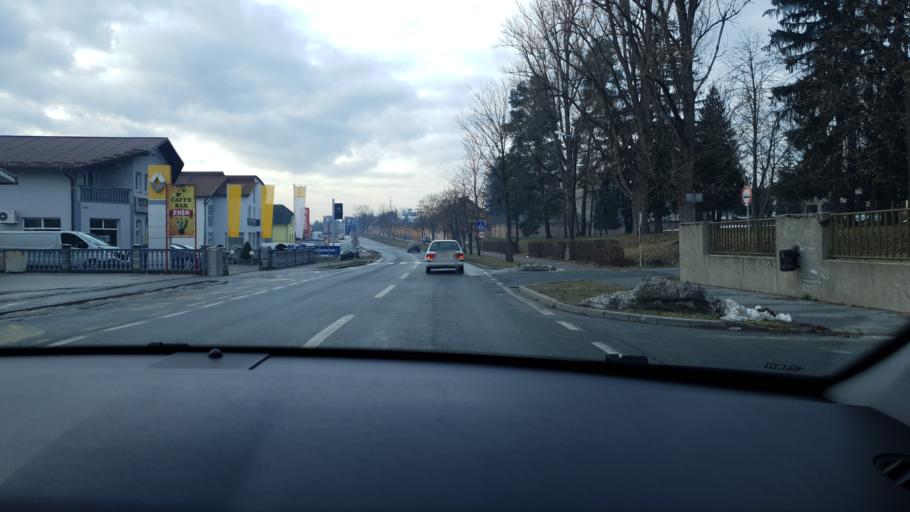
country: HR
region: Pozesko-Slavonska
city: Pozega
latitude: 45.3430
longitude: 17.6976
